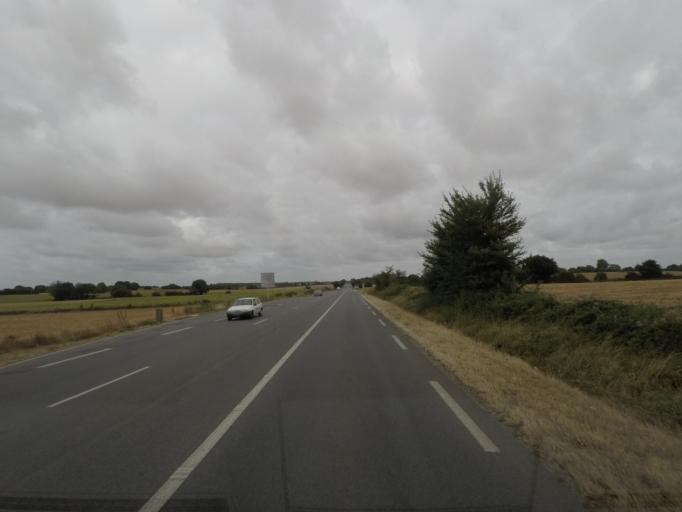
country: FR
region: Poitou-Charentes
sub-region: Departement des Deux-Sevres
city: Thorigne
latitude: 46.2773
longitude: -0.2464
